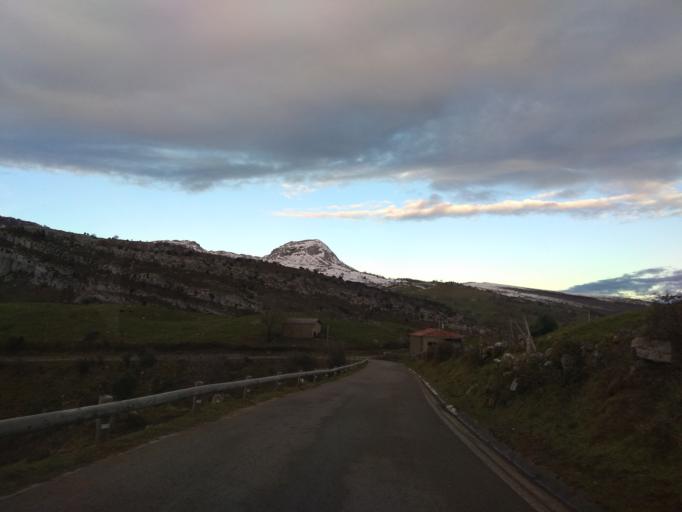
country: ES
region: Cantabria
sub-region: Provincia de Cantabria
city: Arredondo
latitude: 43.2019
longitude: -3.5831
